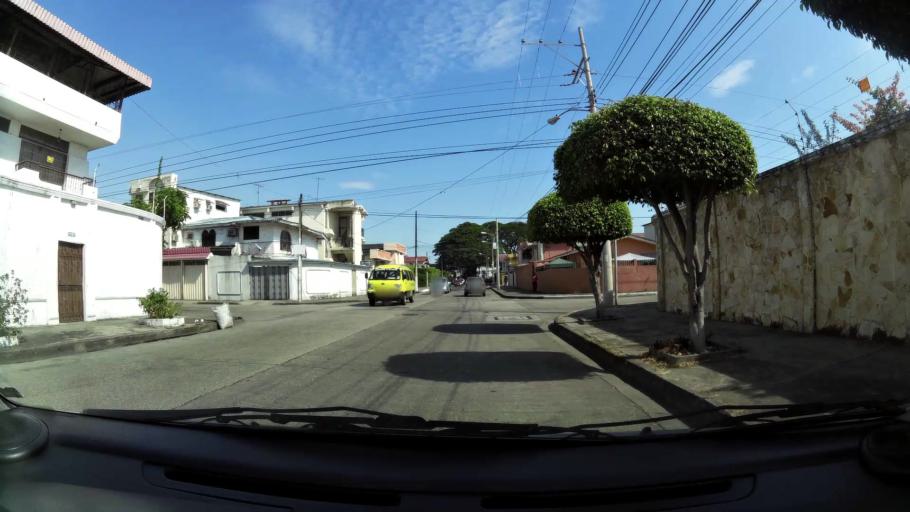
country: EC
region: Guayas
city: Guayaquil
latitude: -2.2242
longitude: -79.8945
